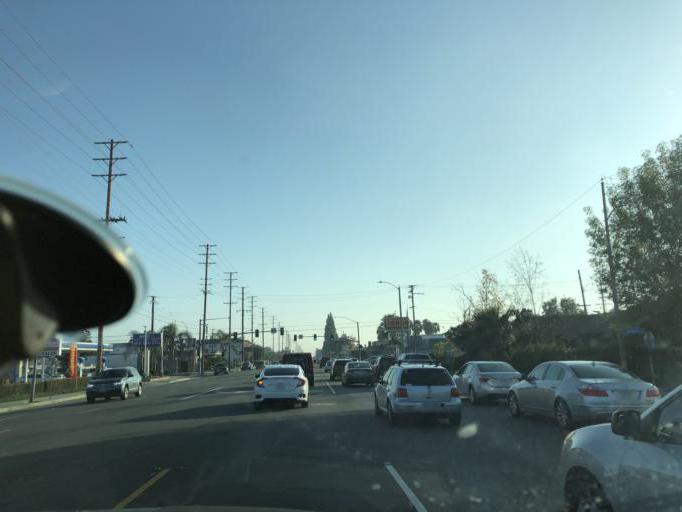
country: US
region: California
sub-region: Orange County
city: Orange
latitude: 33.7852
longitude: -117.8358
